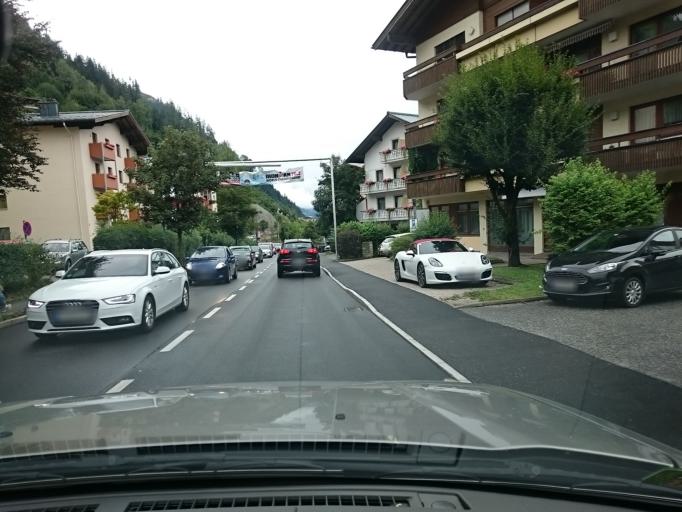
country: AT
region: Salzburg
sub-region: Politischer Bezirk Zell am See
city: Zell am See
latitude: 47.3269
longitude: 12.7966
